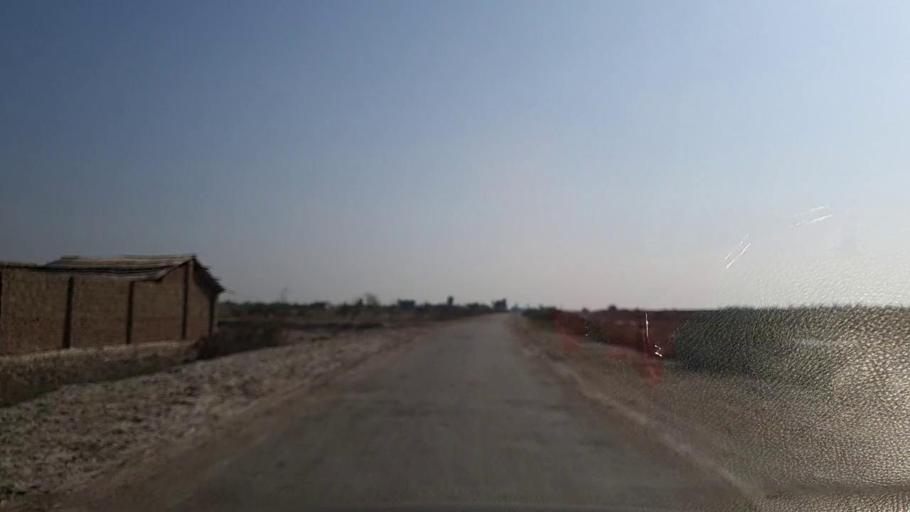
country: PK
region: Sindh
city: Sanghar
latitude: 25.9994
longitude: 69.0238
